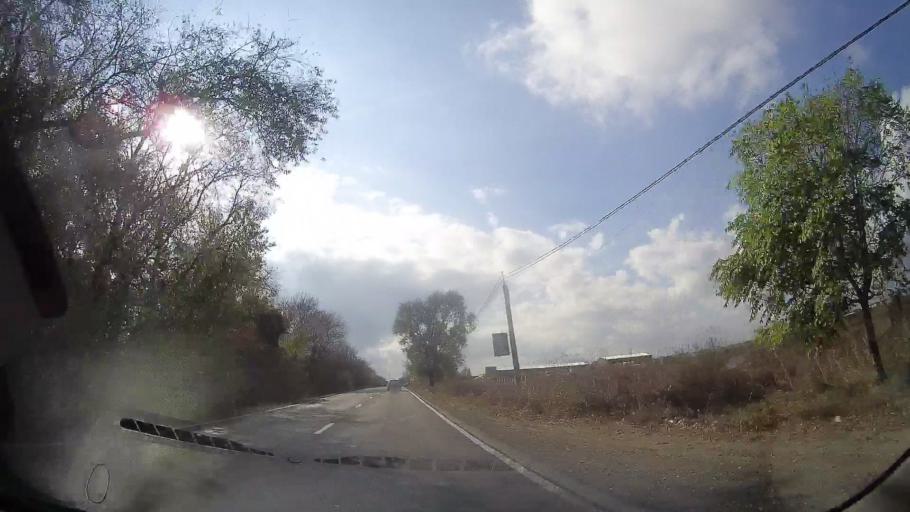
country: RO
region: Constanta
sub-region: Comuna Agigea
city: Agigea
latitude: 44.0840
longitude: 28.6065
